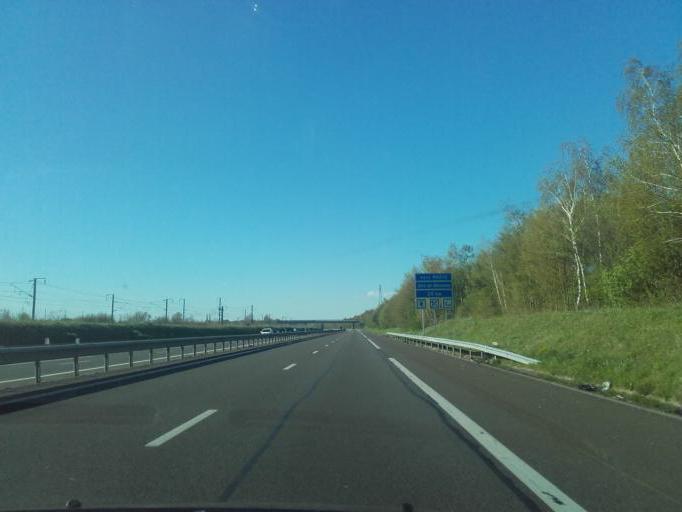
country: FR
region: Rhone-Alpes
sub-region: Departement du Rhone
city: Jons
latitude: 45.7819
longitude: 5.0813
